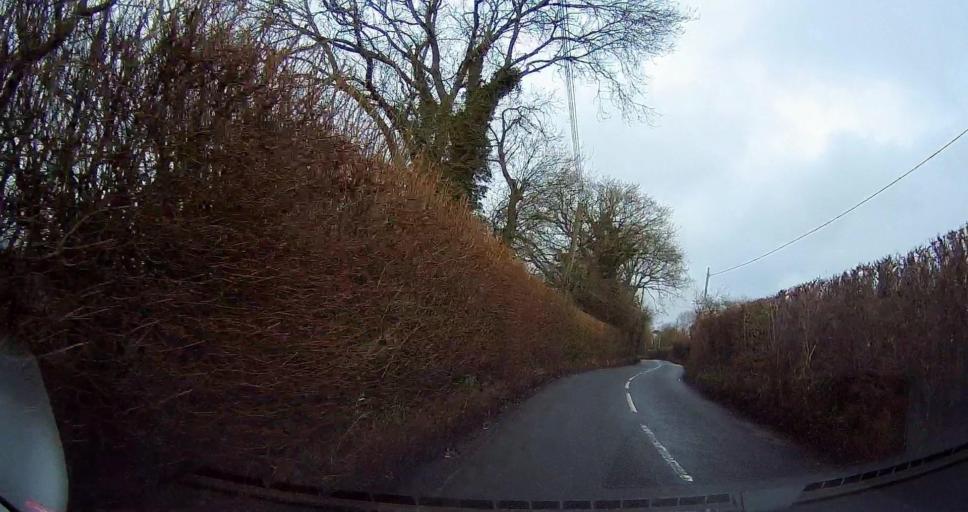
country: GB
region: England
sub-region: Kent
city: Biggin Hill
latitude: 51.3219
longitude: 0.0710
